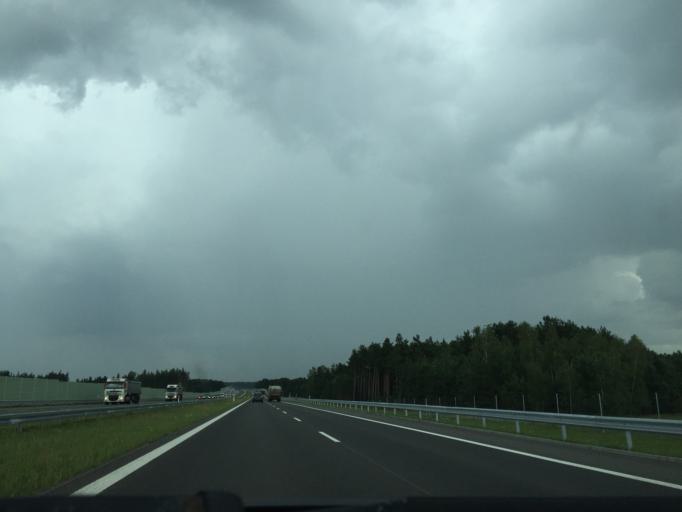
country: PL
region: Masovian Voivodeship
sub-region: Powiat szydlowiecki
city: Oronsko
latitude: 51.3050
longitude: 21.0020
